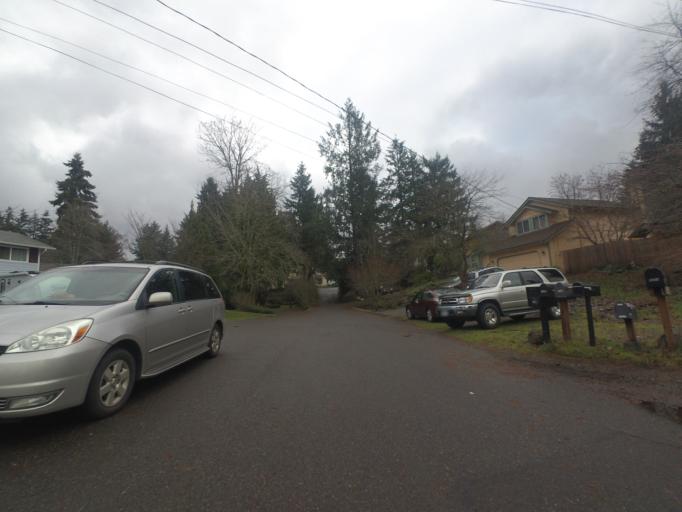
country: US
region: Washington
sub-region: Pierce County
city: University Place
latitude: 47.2194
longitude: -122.5479
